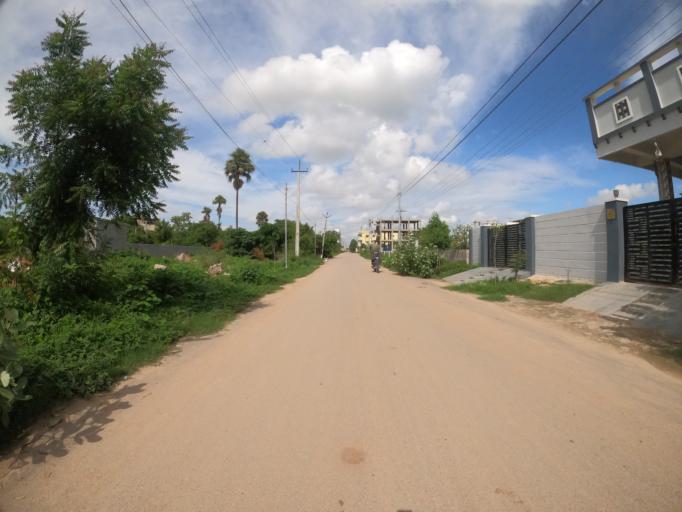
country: IN
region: Telangana
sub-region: Hyderabad
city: Hyderabad
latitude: 17.3517
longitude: 78.3930
